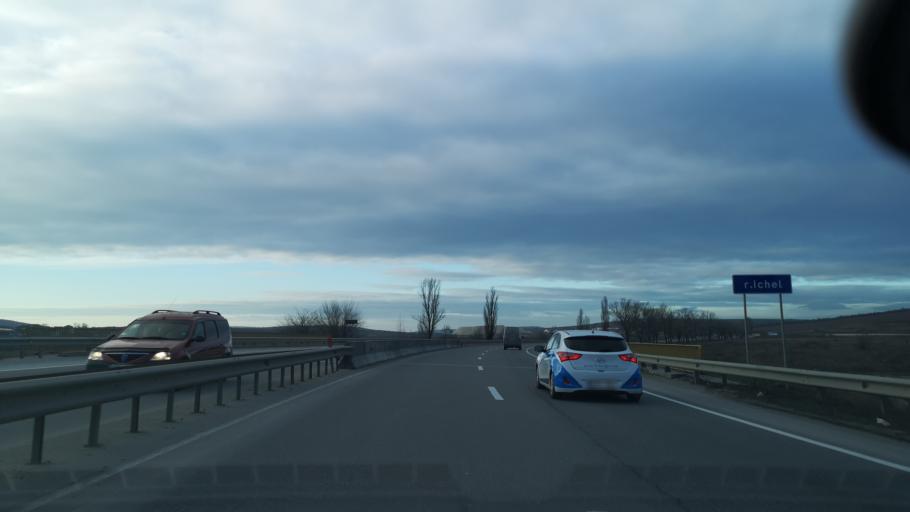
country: MD
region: Chisinau
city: Cricova
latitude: 47.1715
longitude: 28.7998
